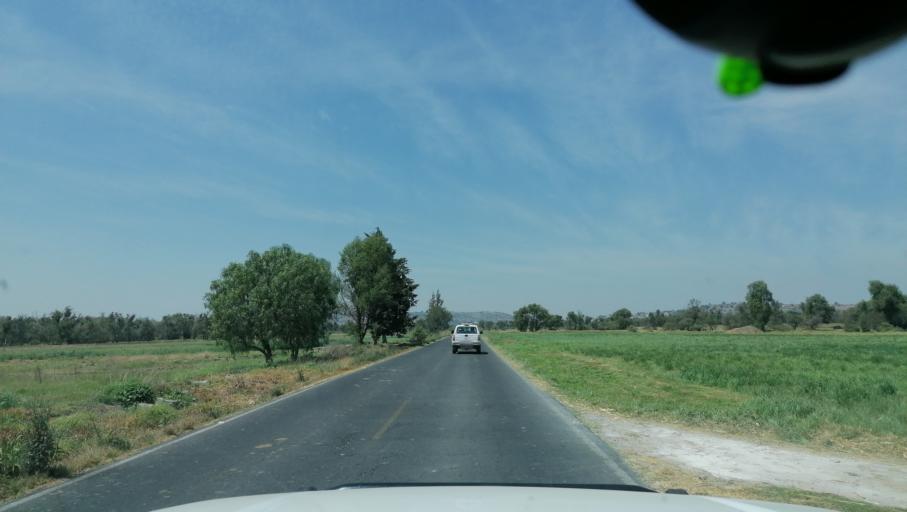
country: MX
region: Tlaxcala
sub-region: Tetlatlahuca
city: Tetlatlahuca
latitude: 19.2107
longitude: -98.2820
